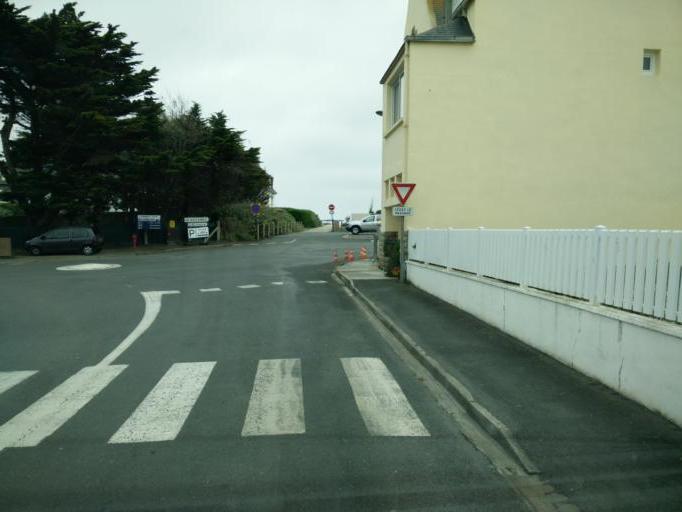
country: FR
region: Brittany
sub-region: Departement du Finistere
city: Plobannalec-Lesconil
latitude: 47.7950
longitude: -4.2204
